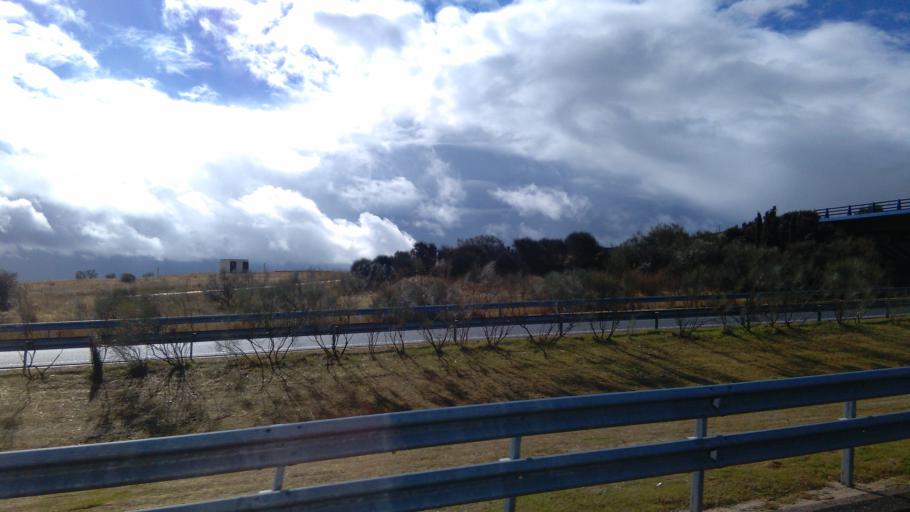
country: ES
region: Madrid
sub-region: Provincia de Madrid
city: Navalcarnero
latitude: 40.2660
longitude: -4.0165
